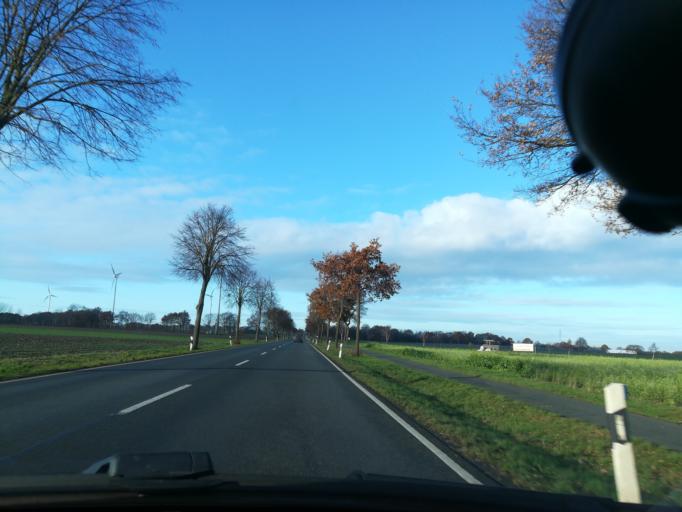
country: DE
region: Lower Saxony
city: Uchte
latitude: 52.4728
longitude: 8.9018
